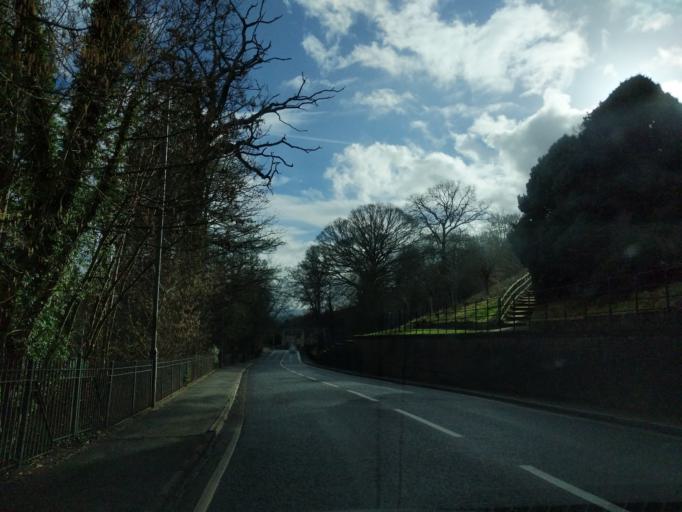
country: GB
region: Scotland
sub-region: South Lanarkshire
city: Carluke
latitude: 55.6952
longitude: -3.8669
